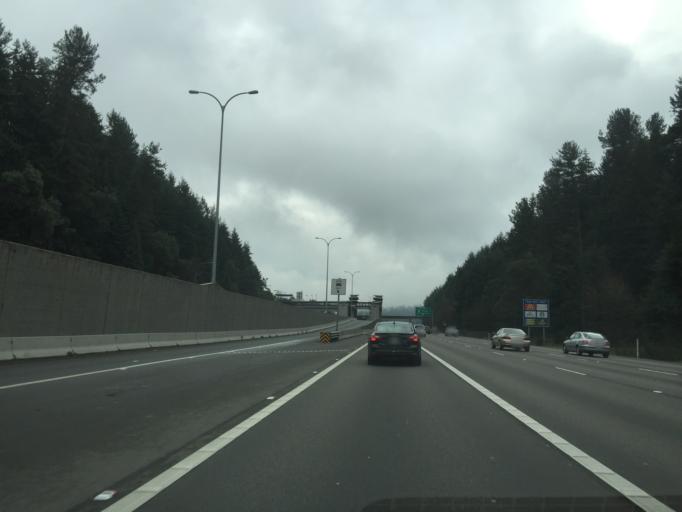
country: US
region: Washington
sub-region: Snohomish County
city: Mountlake Terrace
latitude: 47.7899
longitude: -122.3165
